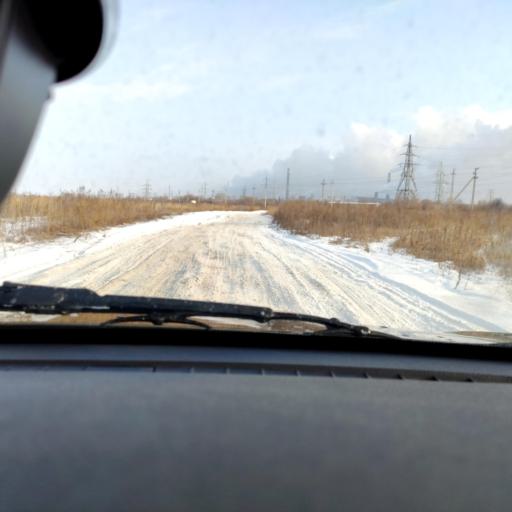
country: RU
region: Samara
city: Tol'yatti
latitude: 53.5446
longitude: 49.4216
